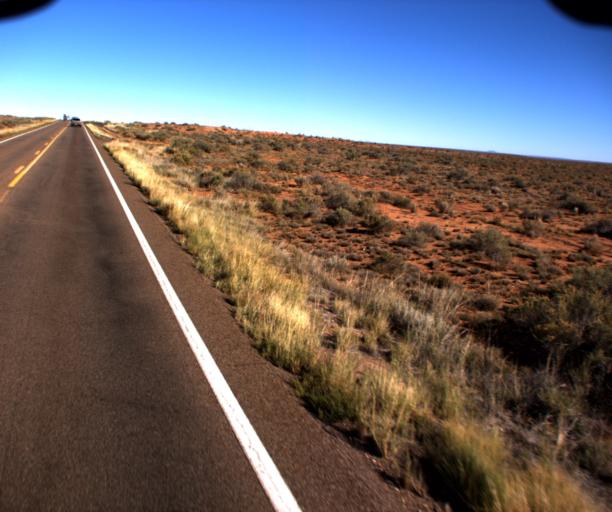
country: US
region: Arizona
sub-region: Navajo County
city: Holbrook
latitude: 34.7329
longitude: -110.1173
